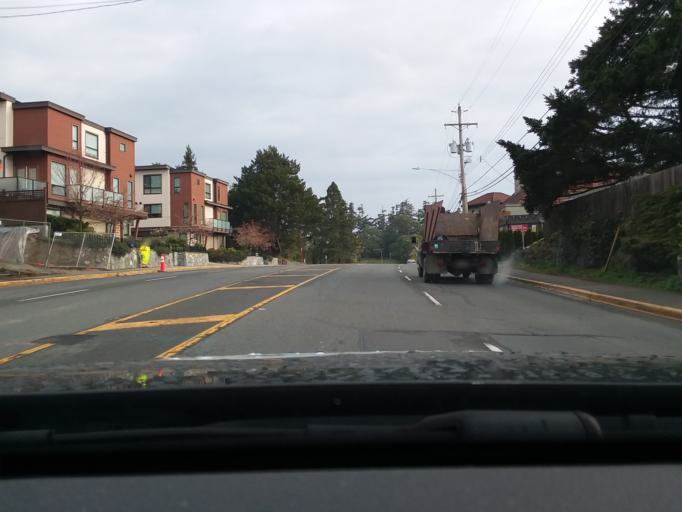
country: CA
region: British Columbia
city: Victoria
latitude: 48.4446
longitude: -123.4013
